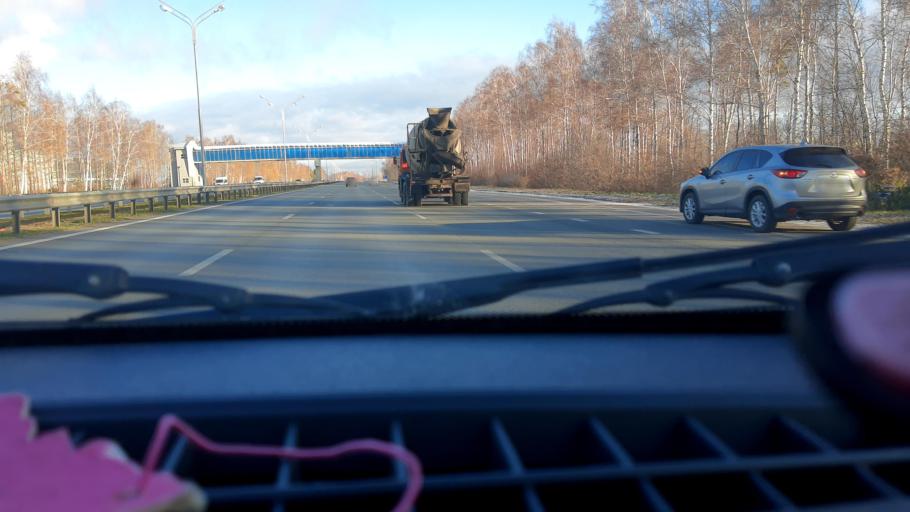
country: RU
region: Bashkortostan
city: Ufa
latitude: 54.5948
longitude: 55.9135
